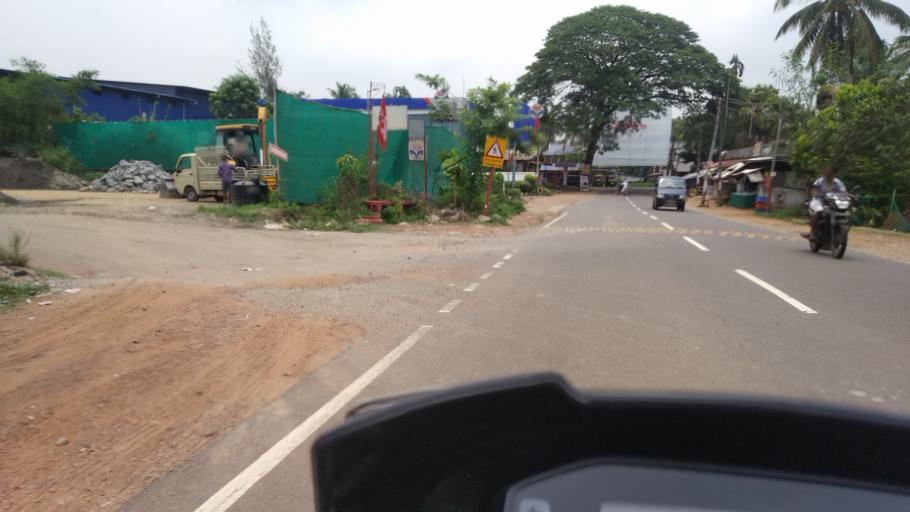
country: IN
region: Kerala
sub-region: Ernakulam
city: Aluva
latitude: 10.1567
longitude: 76.3258
